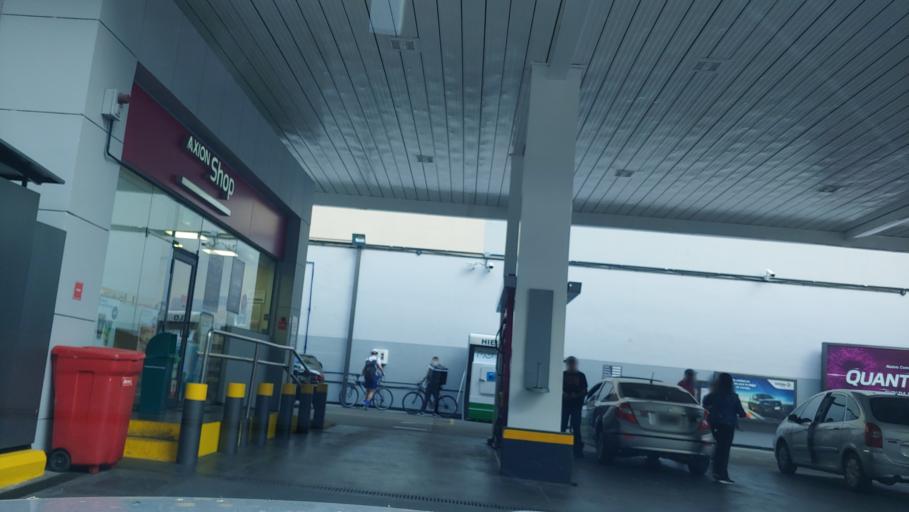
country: AR
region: Buenos Aires F.D.
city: Colegiales
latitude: -34.5699
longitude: -58.4436
